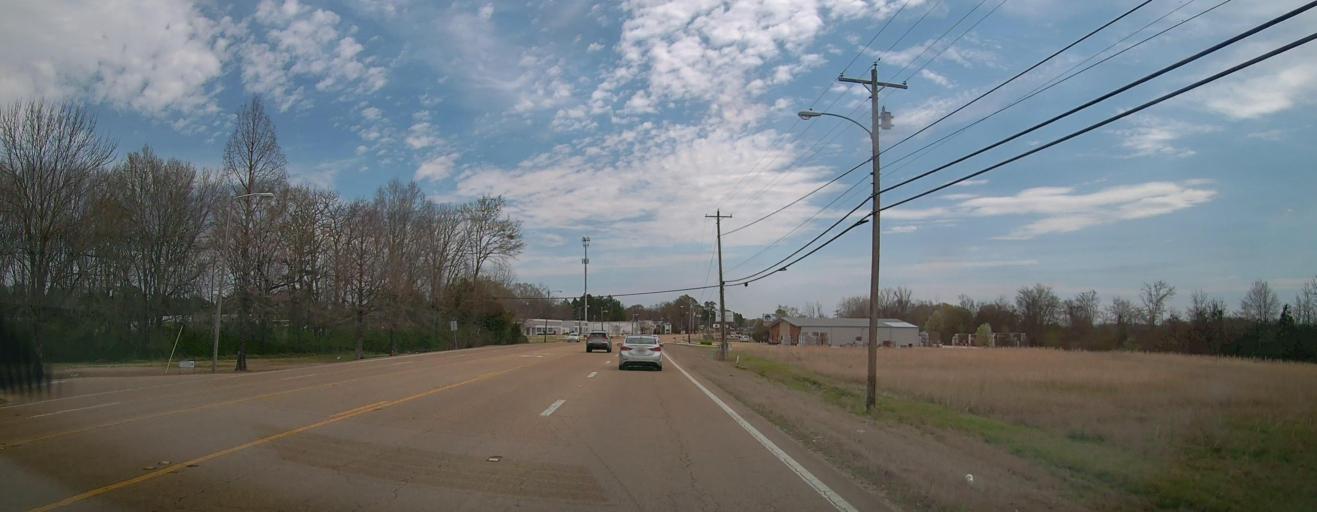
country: US
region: Mississippi
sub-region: Lee County
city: Tupelo
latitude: 34.2910
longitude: -88.7505
